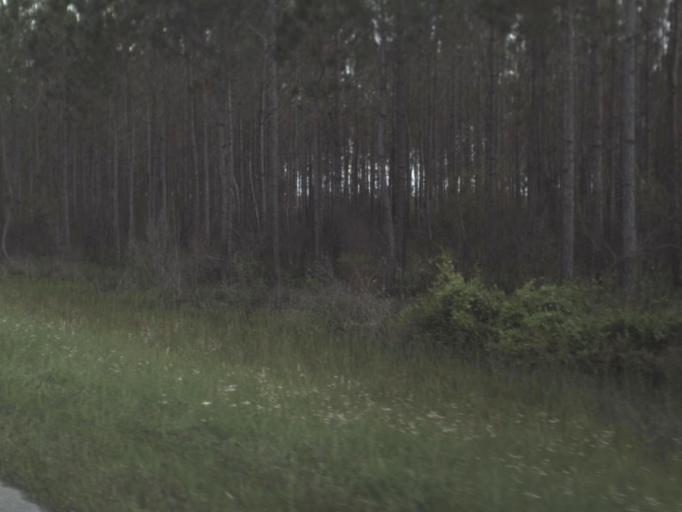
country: US
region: Florida
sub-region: Baker County
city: Macclenny
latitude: 30.5327
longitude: -82.3166
